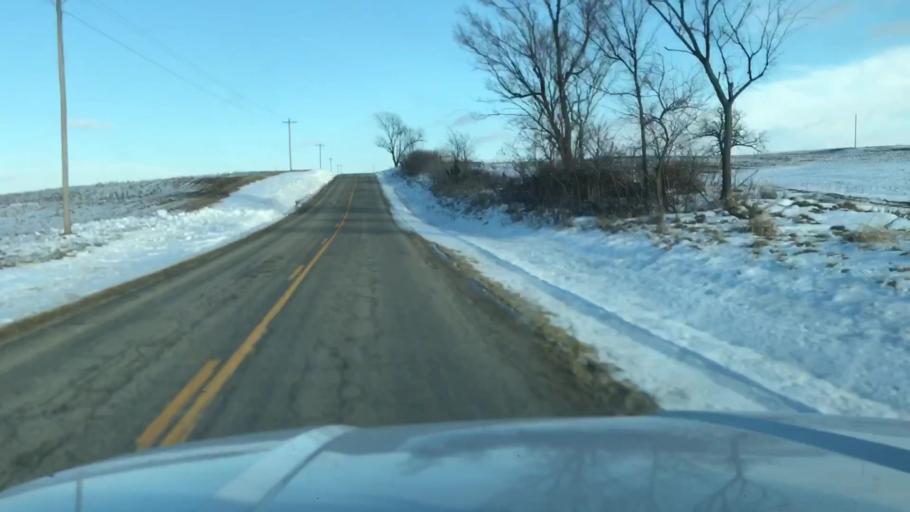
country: US
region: Missouri
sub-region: Holt County
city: Oregon
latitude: 40.1007
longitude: -95.0007
